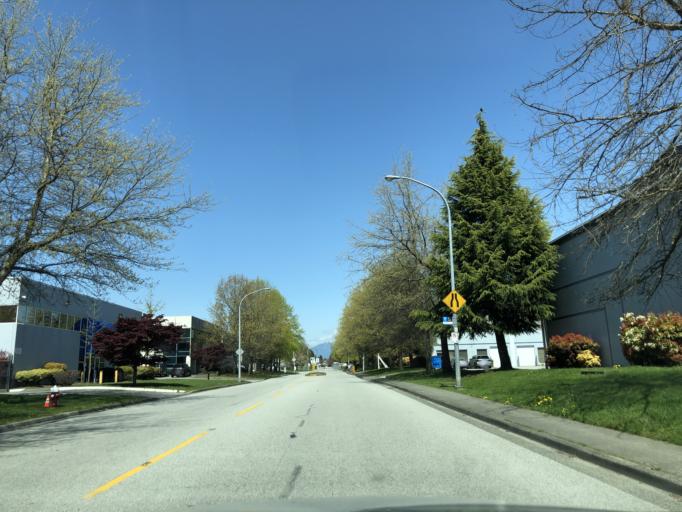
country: CA
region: British Columbia
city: Ladner
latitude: 49.1277
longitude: -123.1005
